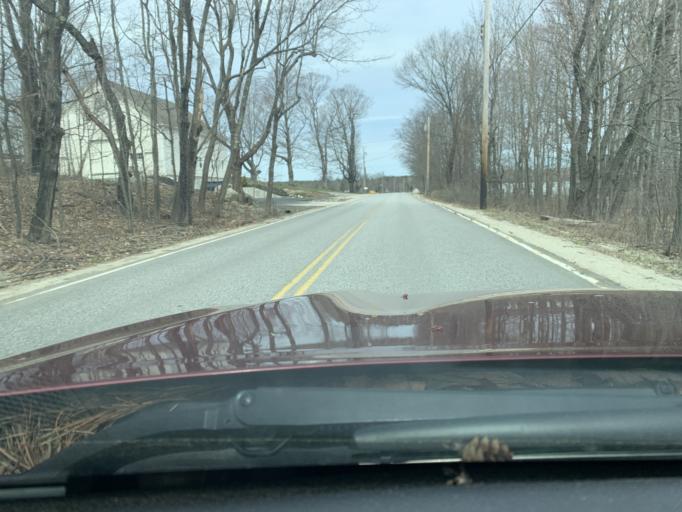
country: US
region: Maine
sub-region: Cumberland County
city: Raymond
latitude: 43.9561
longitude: -70.3876
